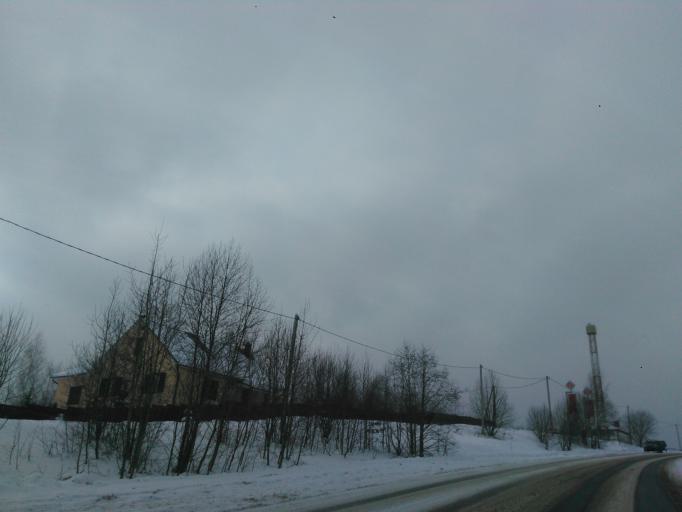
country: RU
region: Moskovskaya
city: Yakhroma
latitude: 56.2675
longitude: 37.4814
